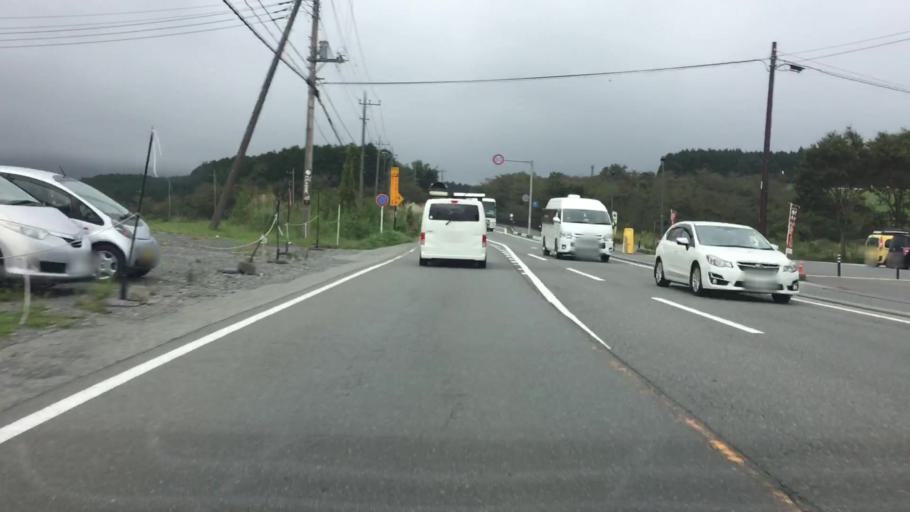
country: JP
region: Yamanashi
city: Fujikawaguchiko
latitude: 35.3852
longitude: 138.5723
